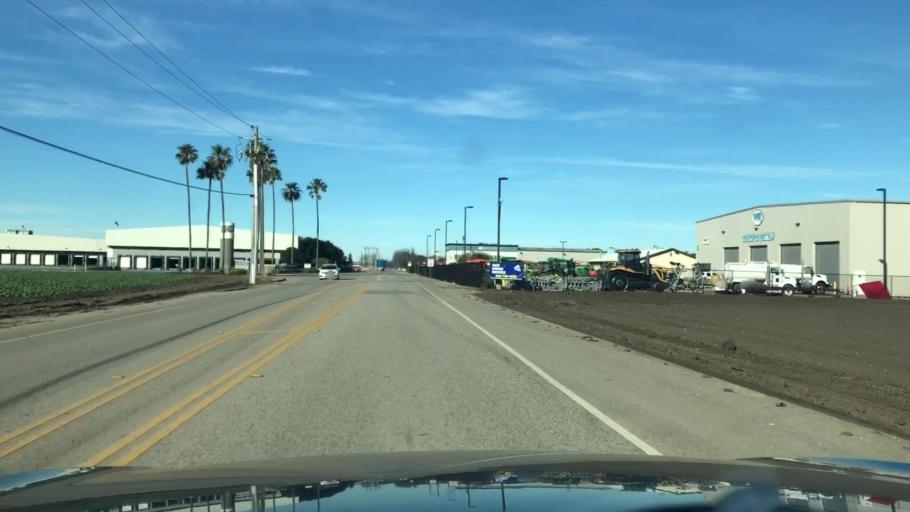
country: US
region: California
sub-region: Monterey County
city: Salinas
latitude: 36.6202
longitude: -121.6416
